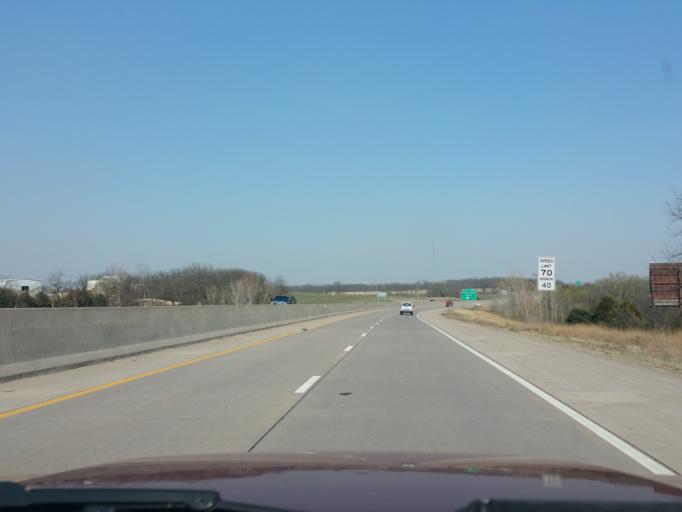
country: US
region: Kansas
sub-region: Shawnee County
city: Silver Lake
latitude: 39.0516
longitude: -95.8060
